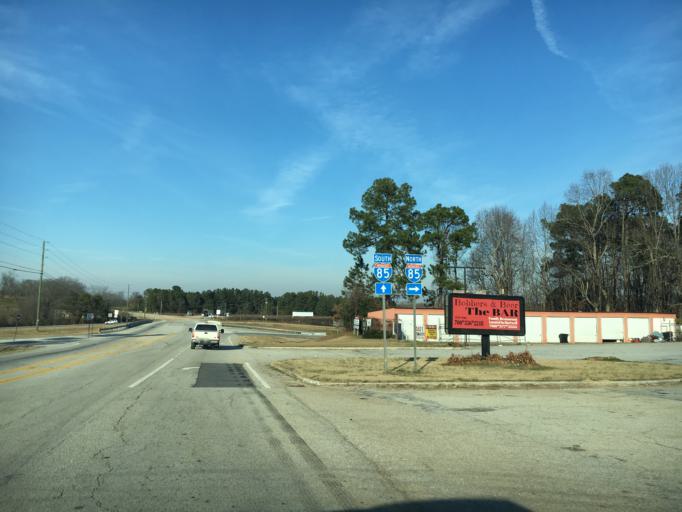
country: US
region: Georgia
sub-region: Franklin County
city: Gumlog
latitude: 34.4723
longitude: -83.0588
